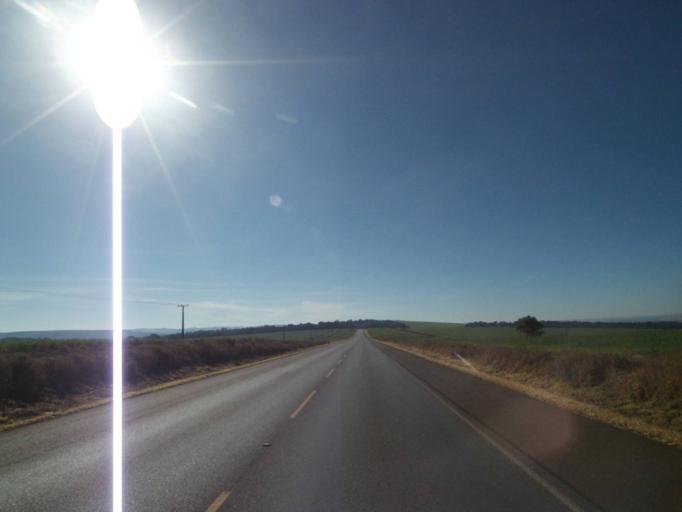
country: BR
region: Parana
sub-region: Tibagi
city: Tibagi
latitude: -24.4308
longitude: -50.4091
